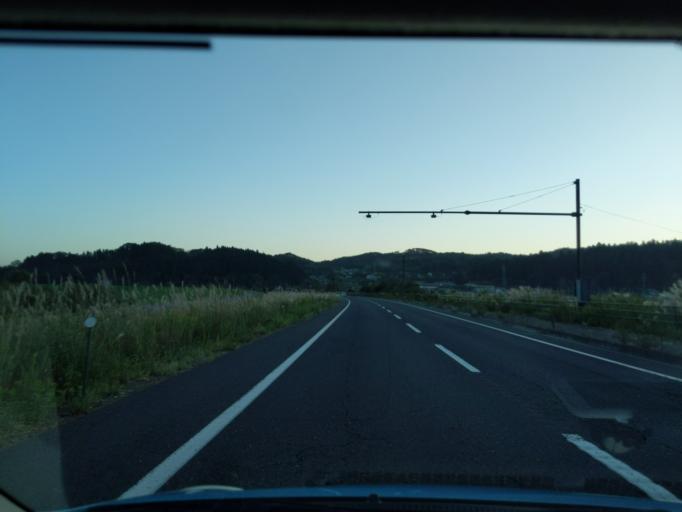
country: JP
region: Iwate
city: Ichinoseki
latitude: 39.0047
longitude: 141.1141
